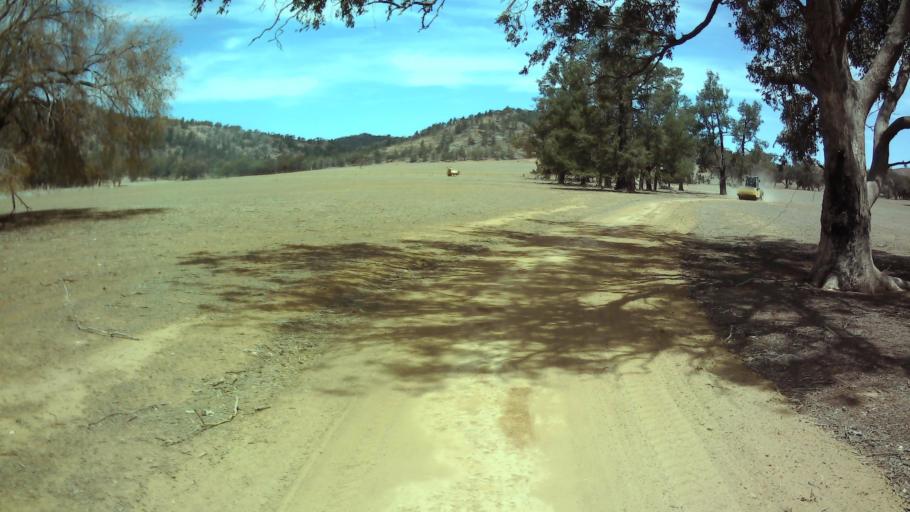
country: AU
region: New South Wales
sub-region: Weddin
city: Grenfell
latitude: -33.7714
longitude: 148.1510
